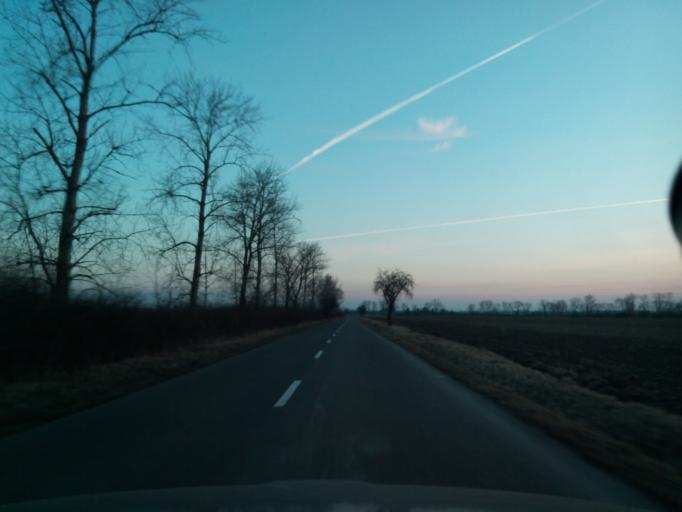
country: SK
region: Kosicky
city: Sobrance
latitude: 48.7684
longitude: 22.1246
